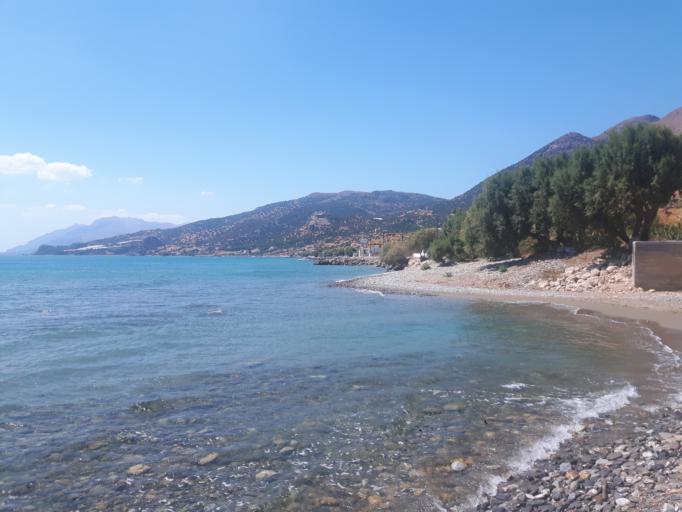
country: GR
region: Crete
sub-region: Nomos Irakleiou
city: Arkalochori
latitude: 34.9976
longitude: 25.3875
